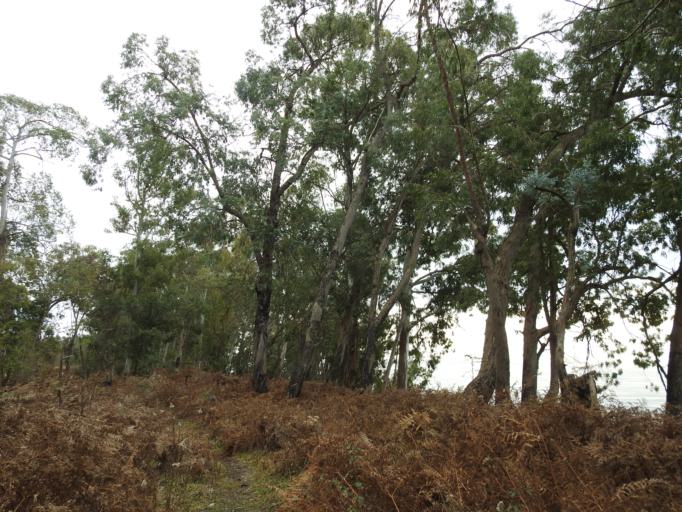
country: GE
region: Abkhazia
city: Dranda
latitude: 42.7933
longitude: 41.2564
